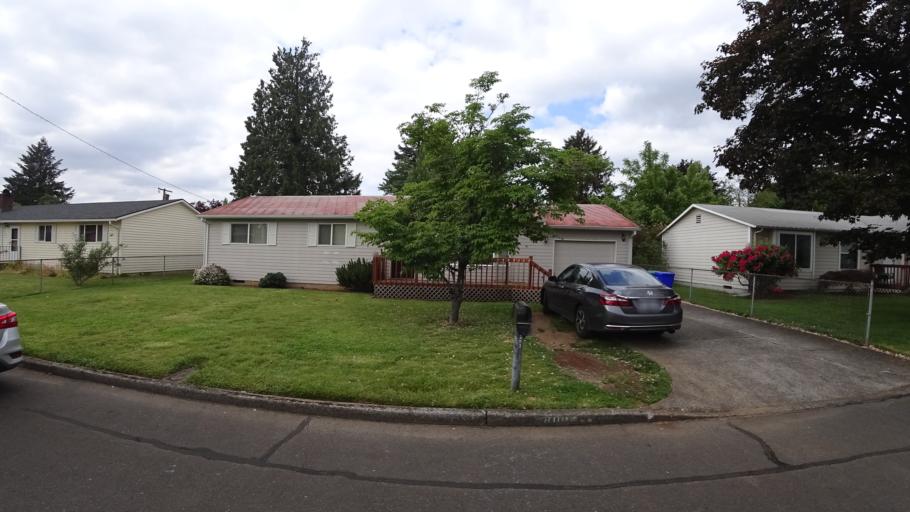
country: US
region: Oregon
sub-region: Multnomah County
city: Gresham
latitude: 45.5106
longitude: -122.4777
